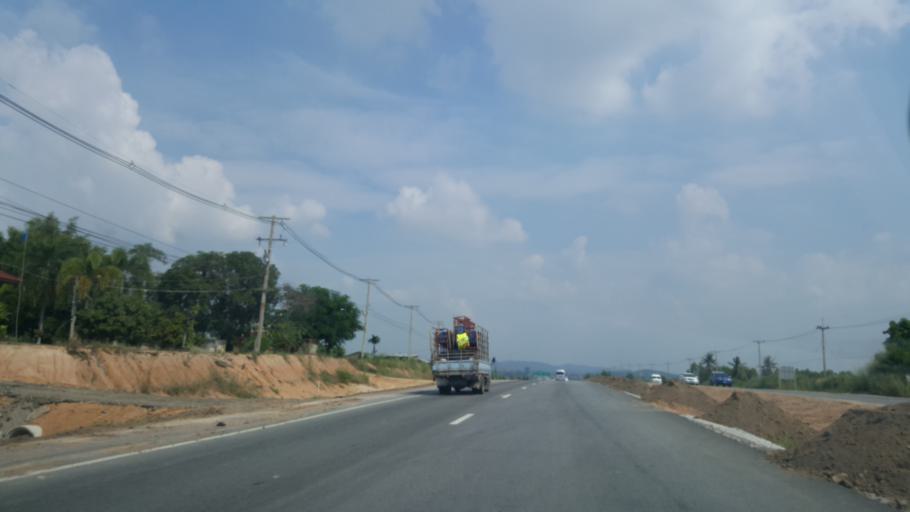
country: TH
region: Chon Buri
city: Phatthaya
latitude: 12.8989
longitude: 101.0270
